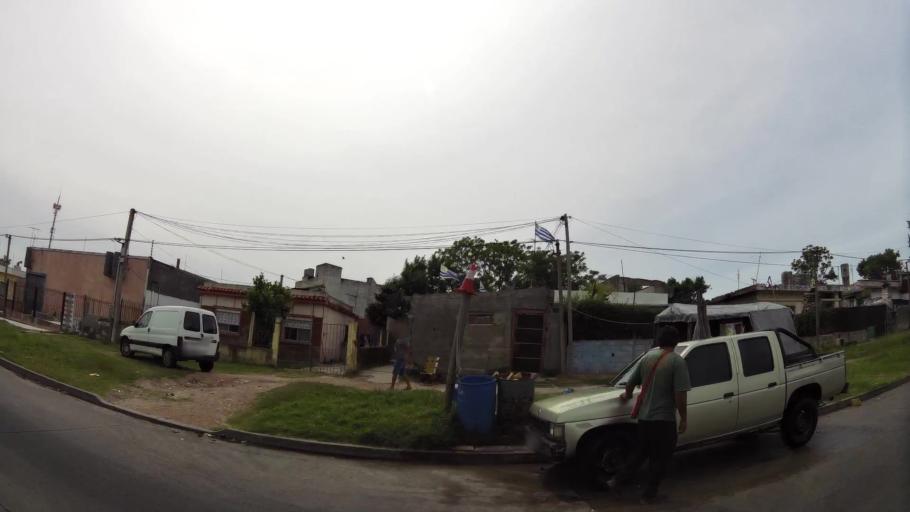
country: UY
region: Montevideo
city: Montevideo
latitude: -34.8403
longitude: -56.1687
